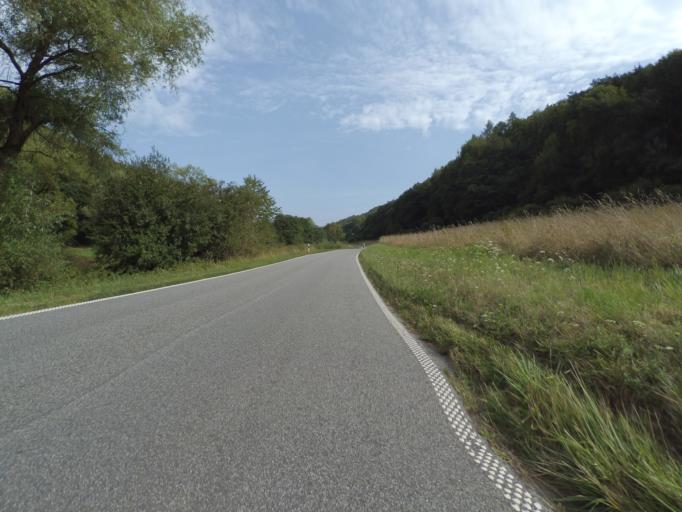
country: DE
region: Rheinland-Pfalz
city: Tawern
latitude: 49.6614
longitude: 6.5126
